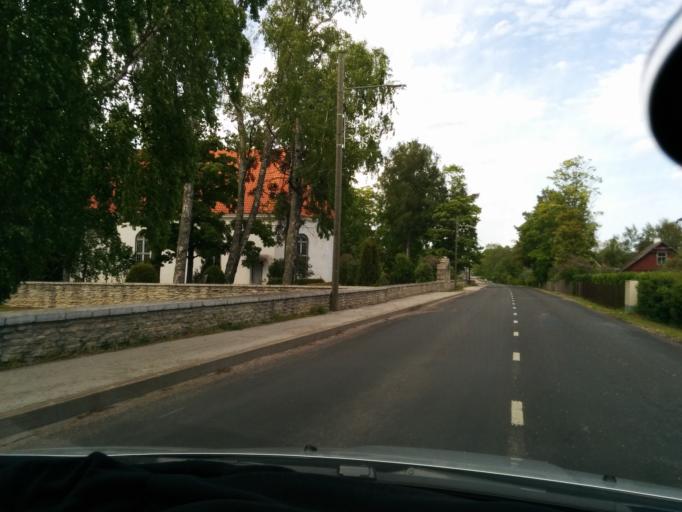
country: EE
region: Harju
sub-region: Loksa linn
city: Loksa
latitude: 59.5747
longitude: 25.7251
